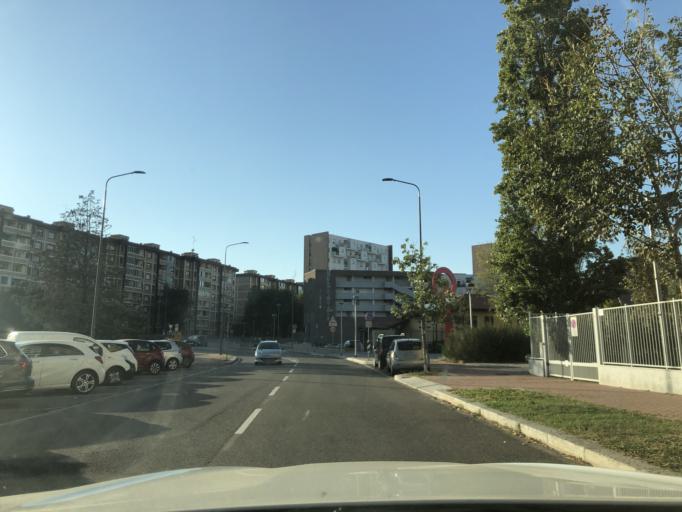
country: IT
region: Lombardy
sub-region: Citta metropolitana di Milano
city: Pero
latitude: 45.5013
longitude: 9.1086
